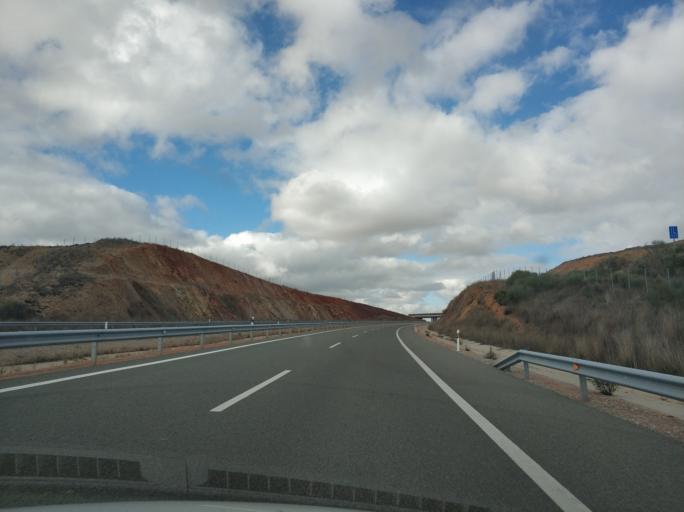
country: ES
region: Castille and Leon
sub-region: Provincia de Soria
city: Yelo
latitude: 41.2311
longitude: -2.4773
